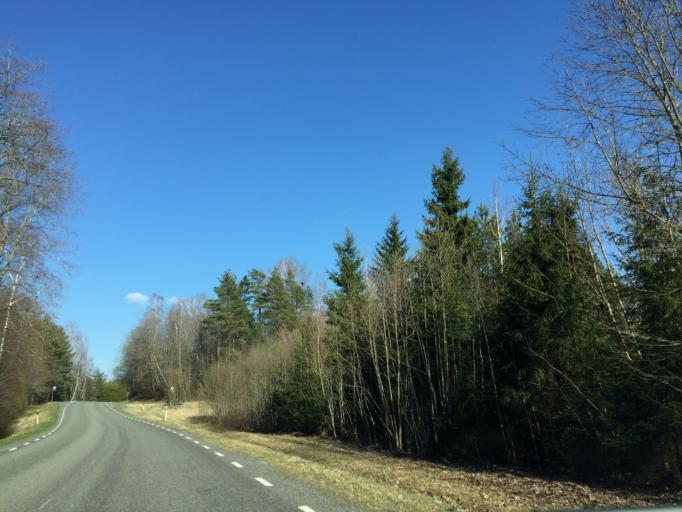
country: EE
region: Viljandimaa
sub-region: Viiratsi vald
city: Viiratsi
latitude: 58.2683
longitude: 25.6646
